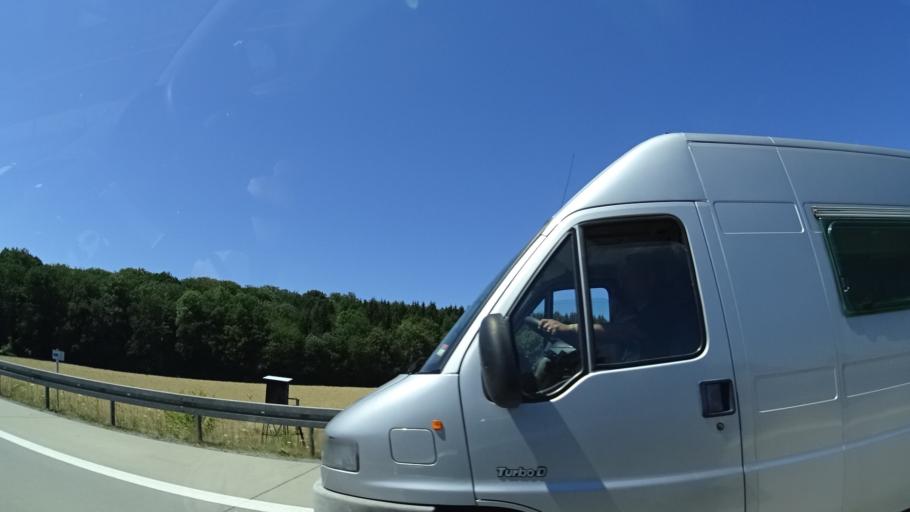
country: DE
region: Bavaria
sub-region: Regierungsbezirk Unterfranken
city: Strahlungen
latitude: 50.2866
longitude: 10.2615
